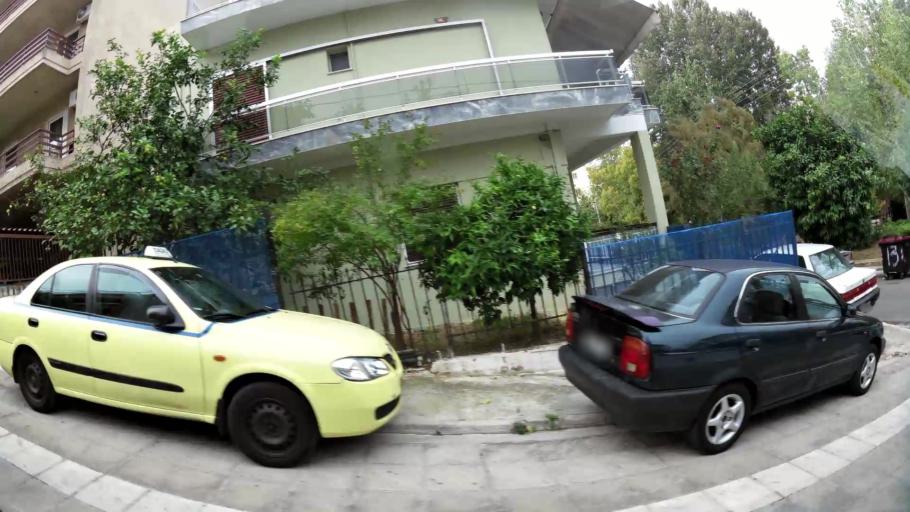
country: GR
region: Attica
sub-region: Nomarchia Athinas
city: Chaidari
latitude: 38.0064
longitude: 23.6674
